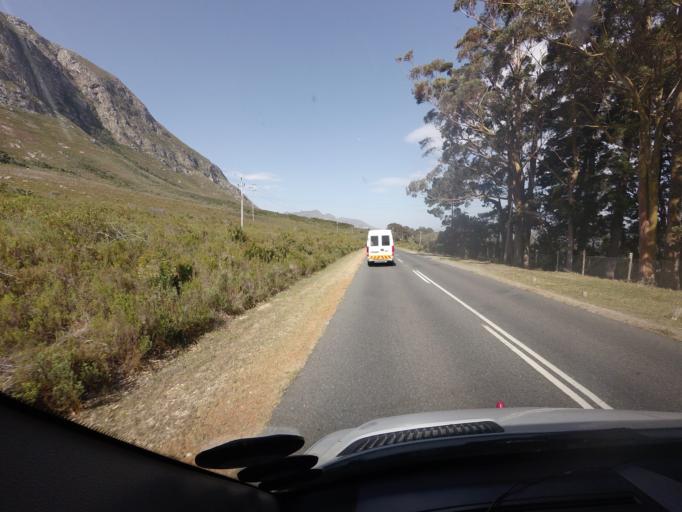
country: ZA
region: Western Cape
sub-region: Overberg District Municipality
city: Hermanus
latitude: -34.4062
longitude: 19.3442
